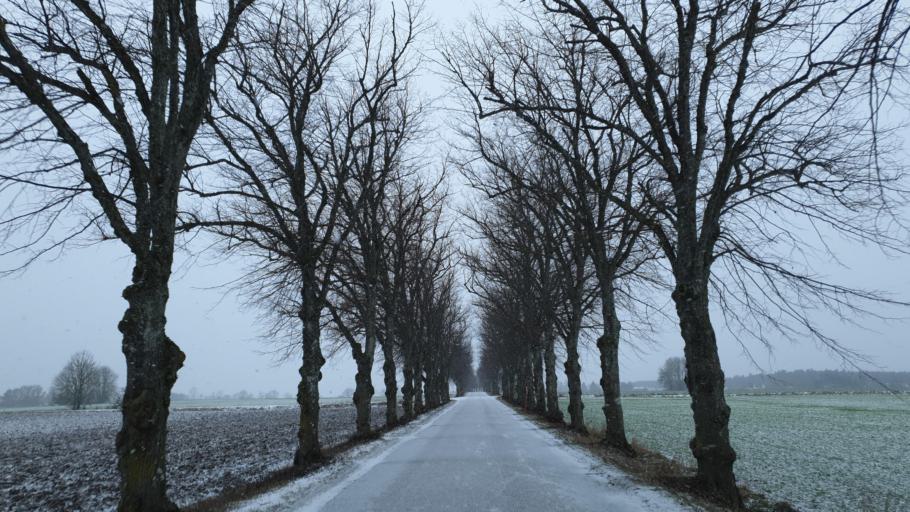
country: SE
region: Gotland
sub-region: Gotland
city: Visby
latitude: 57.5160
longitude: 18.4553
